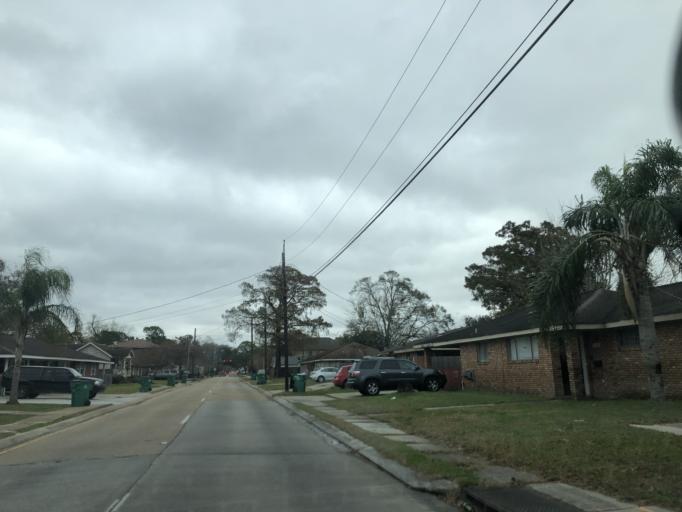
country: US
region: Louisiana
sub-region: Jefferson Parish
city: Metairie Terrace
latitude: 29.9815
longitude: -90.1631
